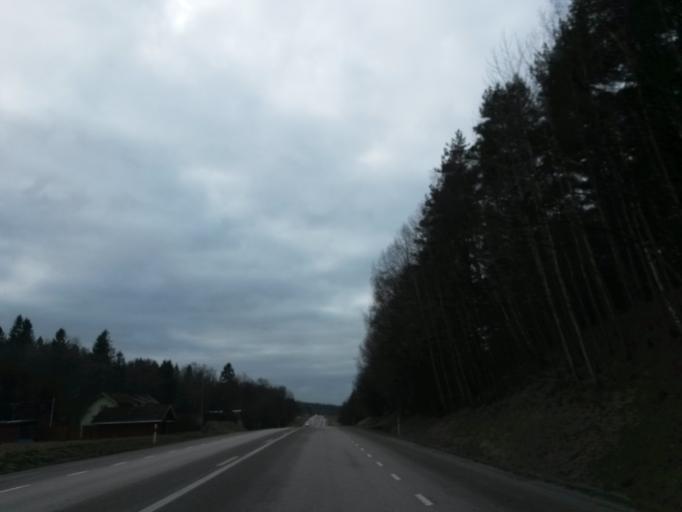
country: SE
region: Vaestra Goetaland
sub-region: Alingsas Kommun
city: Alingsas
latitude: 57.9455
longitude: 12.5959
